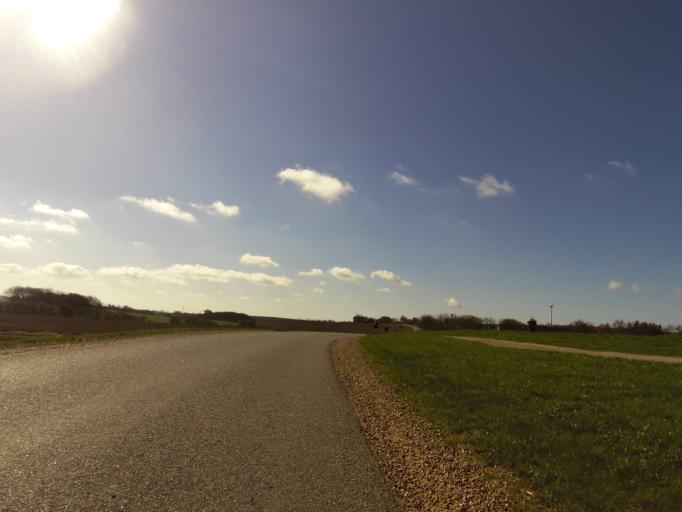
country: DK
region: Central Jutland
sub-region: Holstebro Kommune
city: Vinderup
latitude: 56.4623
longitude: 8.7218
